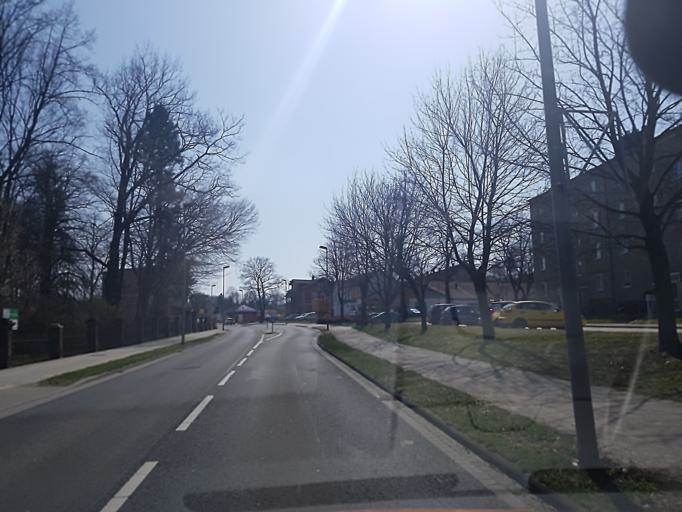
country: DE
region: Brandenburg
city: Tschernitz
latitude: 51.6177
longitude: 14.5938
